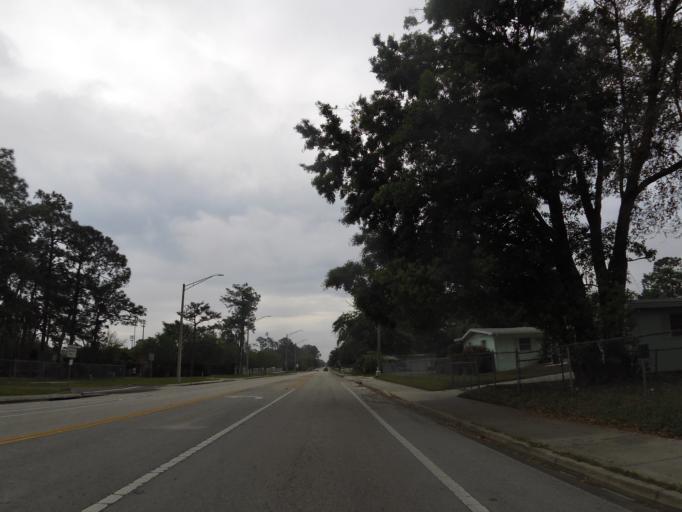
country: US
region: Florida
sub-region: Duval County
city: Jacksonville
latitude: 30.2779
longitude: -81.6166
